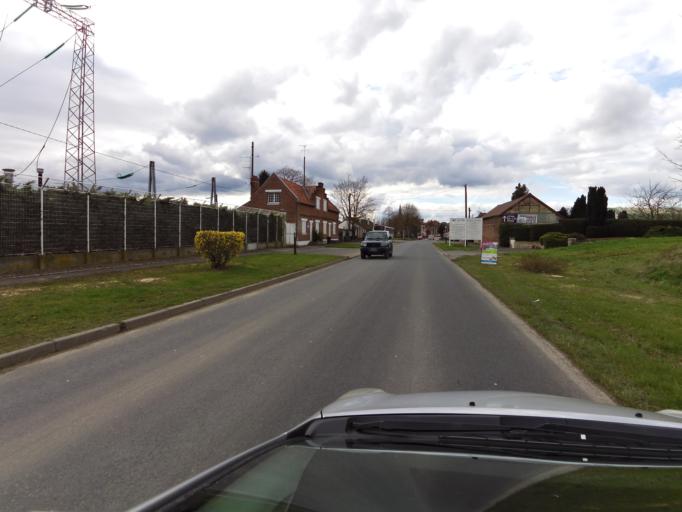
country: FR
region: Picardie
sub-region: Departement de la Somme
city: Roye
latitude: 49.6949
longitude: 2.8008
